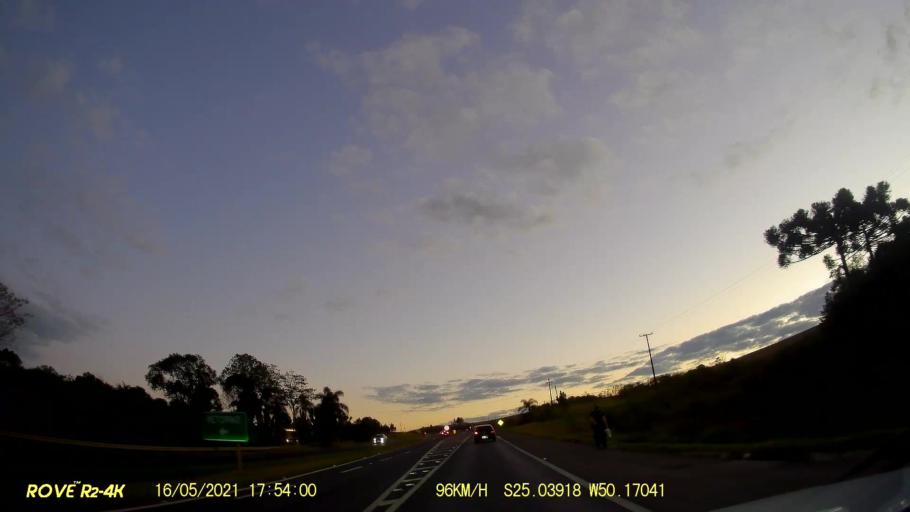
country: BR
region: Parana
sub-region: Ponta Grossa
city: Ponta Grossa
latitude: -25.0393
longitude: -50.1707
